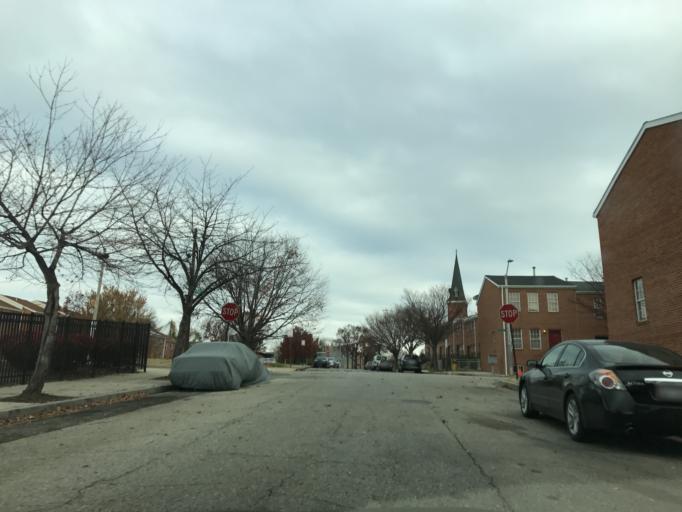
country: US
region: Maryland
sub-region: City of Baltimore
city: Baltimore
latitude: 39.3025
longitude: -76.6021
